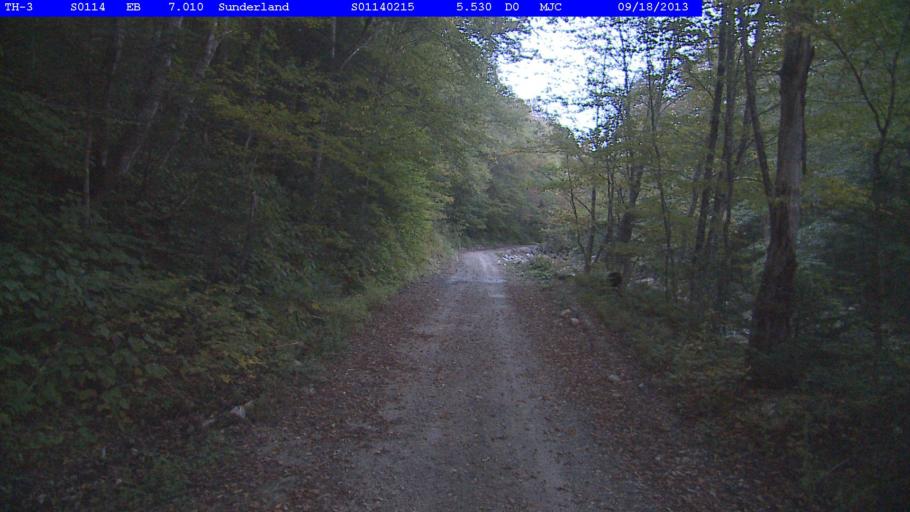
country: US
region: Vermont
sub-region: Bennington County
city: Arlington
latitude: 43.0552
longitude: -73.0705
